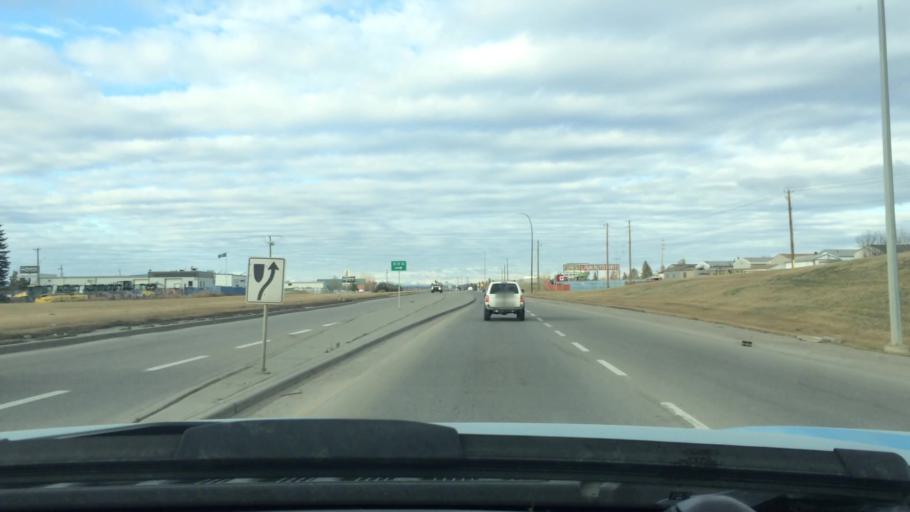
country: CA
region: Alberta
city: Calgary
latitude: 51.0151
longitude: -113.9790
